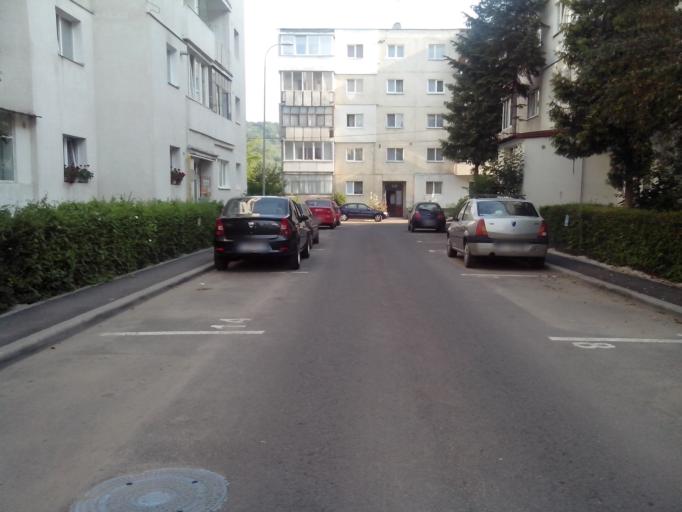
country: RO
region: Cluj
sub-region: Comuna Baciu
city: Baciu
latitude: 46.7597
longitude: 23.5458
